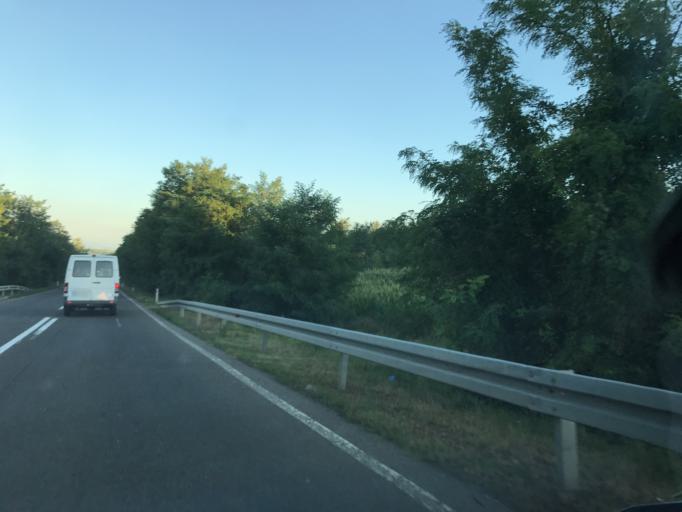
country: RS
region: Central Serbia
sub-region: Branicevski Okrug
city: Pozarevac
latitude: 44.6530
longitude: 21.2037
